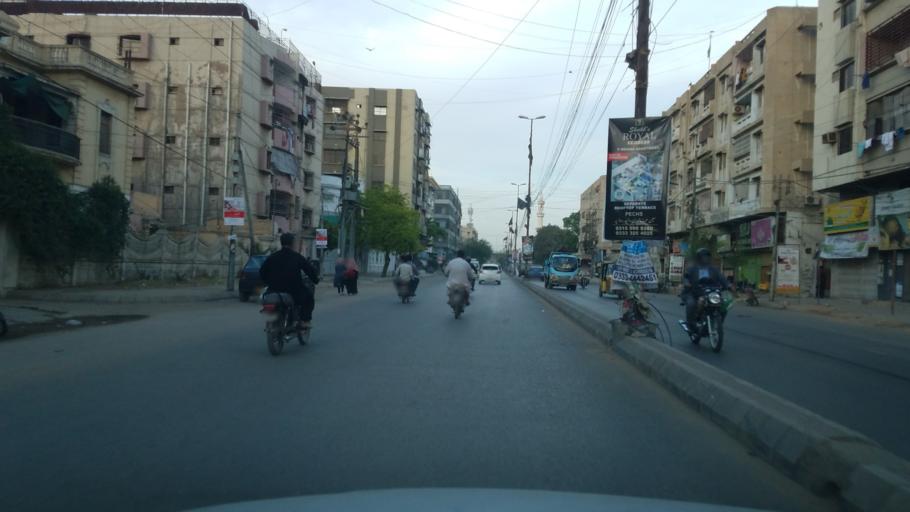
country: PK
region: Sindh
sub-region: Karachi District
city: Karachi
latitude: 24.8778
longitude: 67.0356
